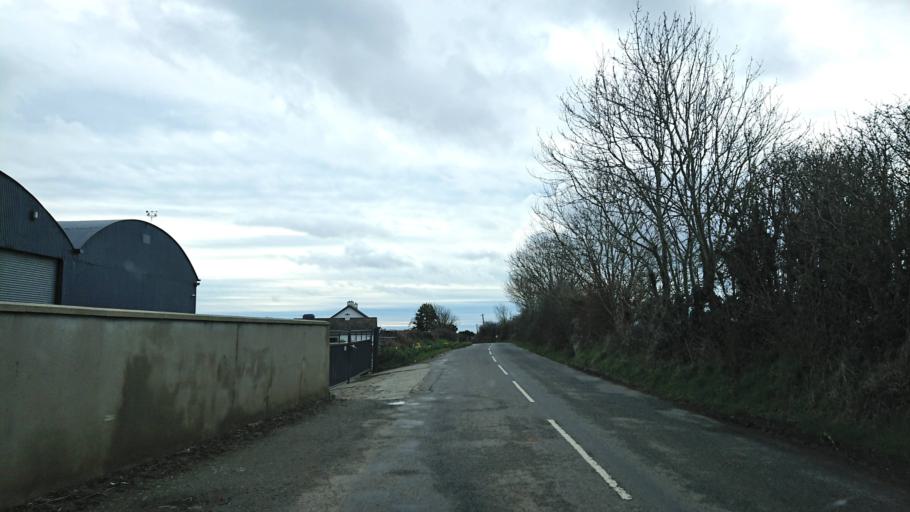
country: IE
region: Munster
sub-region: Waterford
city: Dunmore East
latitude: 52.2421
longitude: -6.9077
